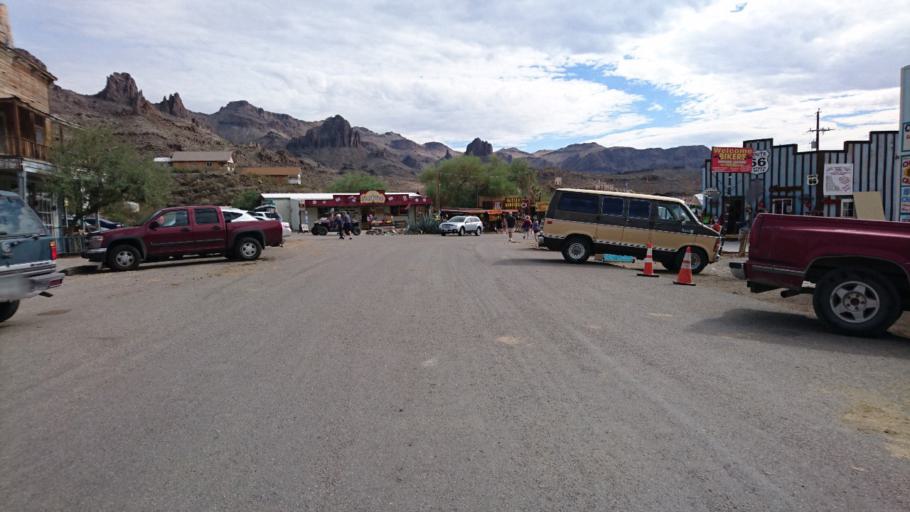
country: US
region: Arizona
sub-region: Mohave County
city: Bullhead City
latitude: 35.0258
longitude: -114.3831
